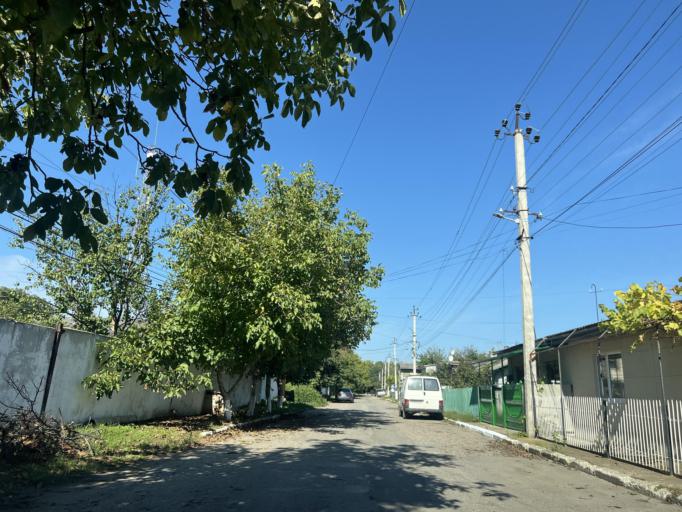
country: RO
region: Iasi
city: Ungheni-Prut
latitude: 47.1972
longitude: 27.7936
